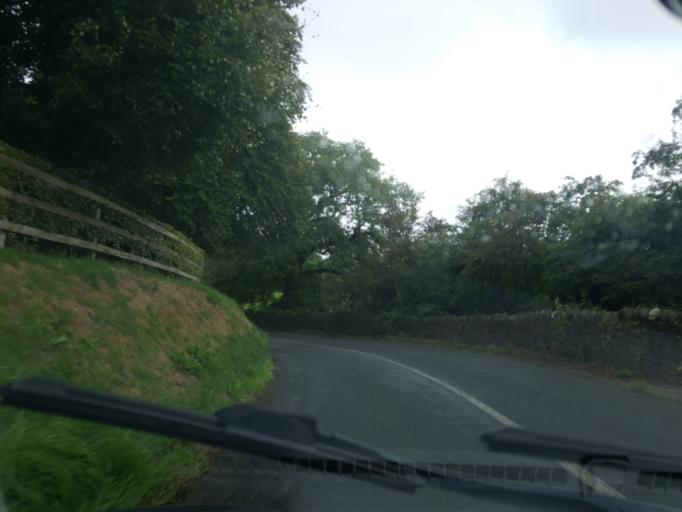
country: IE
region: Leinster
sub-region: Wicklow
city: Valleymount
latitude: 53.1215
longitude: -6.6414
